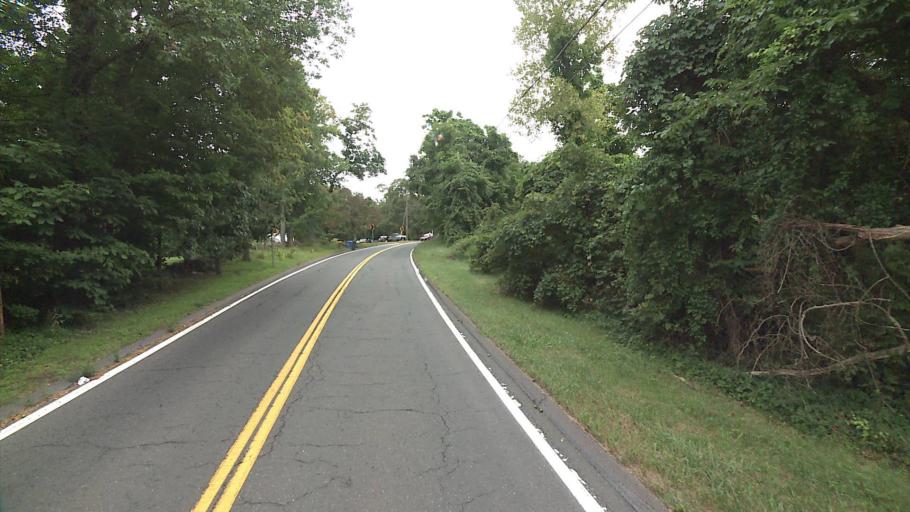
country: US
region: Connecticut
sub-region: Hartford County
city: Manchester
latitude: 41.7980
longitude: -72.4734
